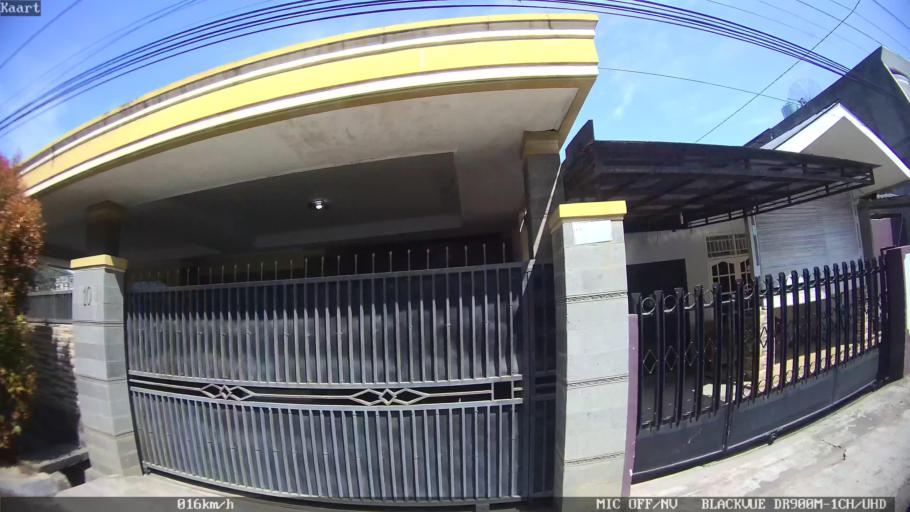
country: ID
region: Lampung
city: Kedaton
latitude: -5.3710
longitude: 105.2468
